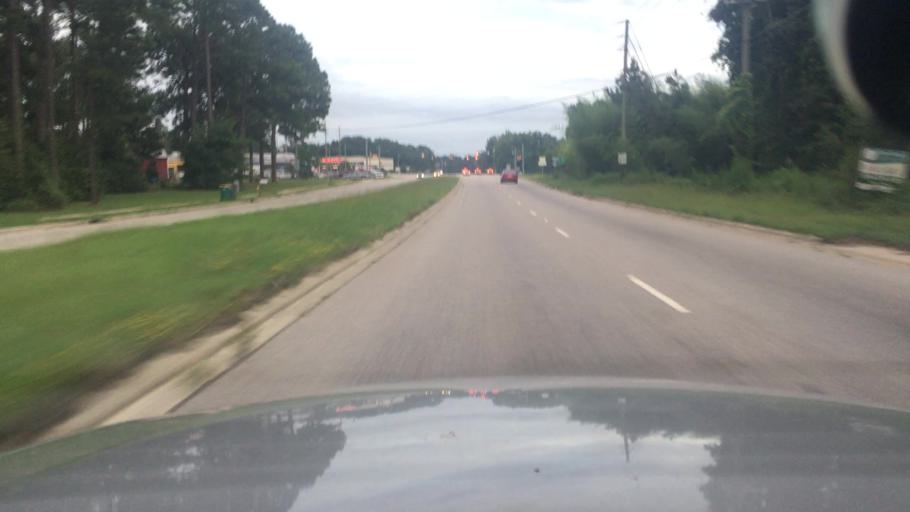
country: US
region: North Carolina
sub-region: Cumberland County
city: Hope Mills
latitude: 34.9973
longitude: -78.9706
